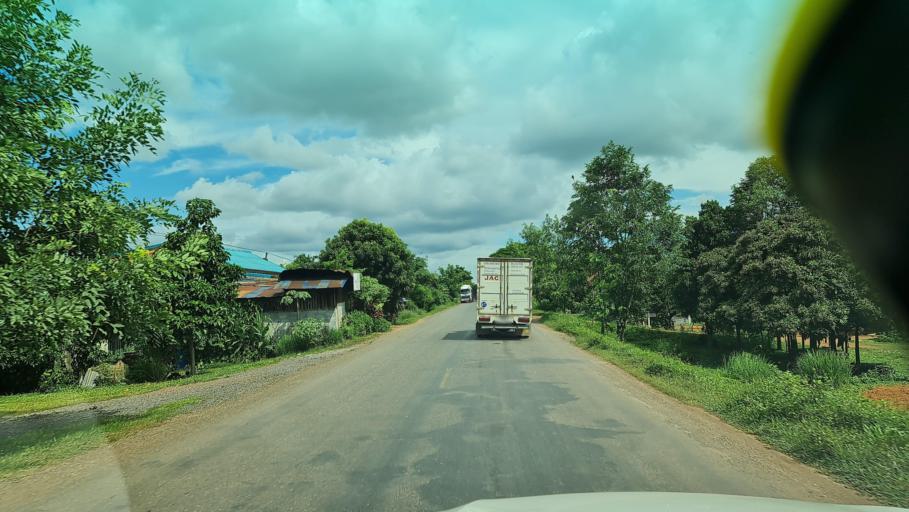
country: LA
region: Bolikhamxai
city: Ban Nahin
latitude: 18.1924
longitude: 104.2212
